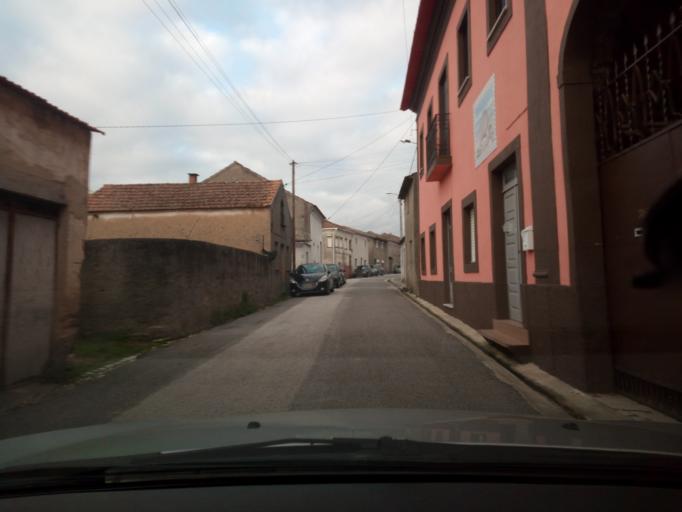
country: PT
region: Aveiro
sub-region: Oliveira do Bairro
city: Oliveira do Bairro
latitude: 40.5468
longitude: -8.4894
